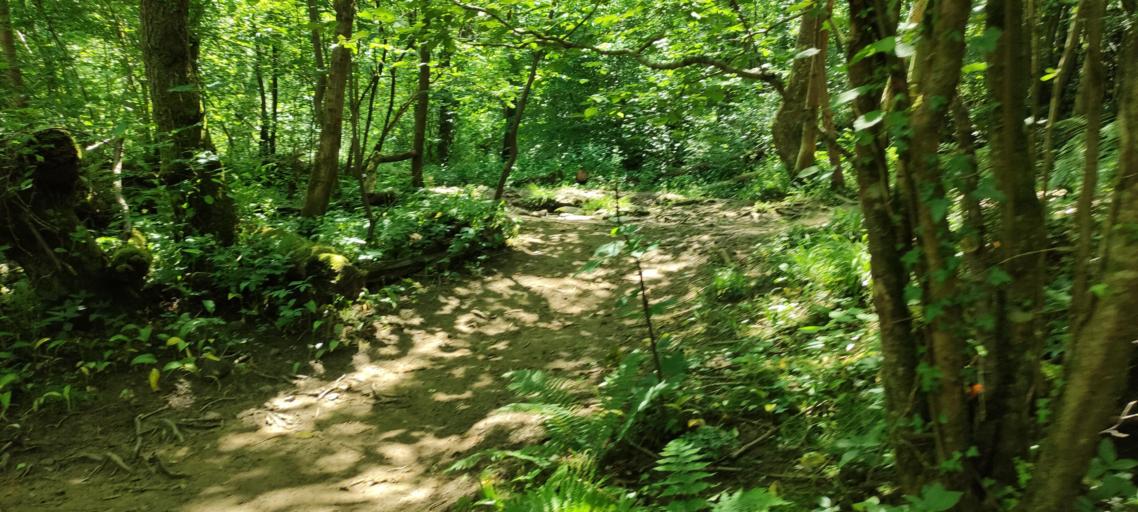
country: GB
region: England
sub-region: North Yorkshire
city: Bedale
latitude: 54.1900
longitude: -1.6401
